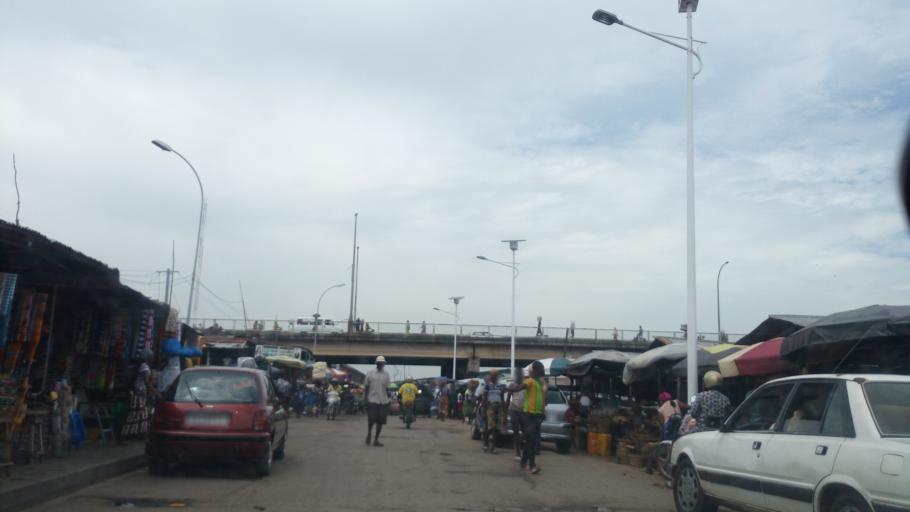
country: BJ
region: Littoral
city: Cotonou
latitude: 6.3701
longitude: 2.4358
